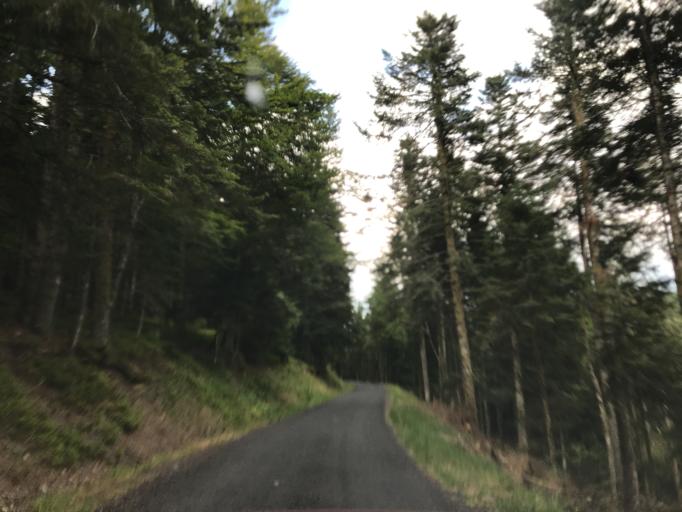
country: FR
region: Rhone-Alpes
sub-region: Departement de la Loire
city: Noiretable
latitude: 45.7616
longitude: 3.7300
